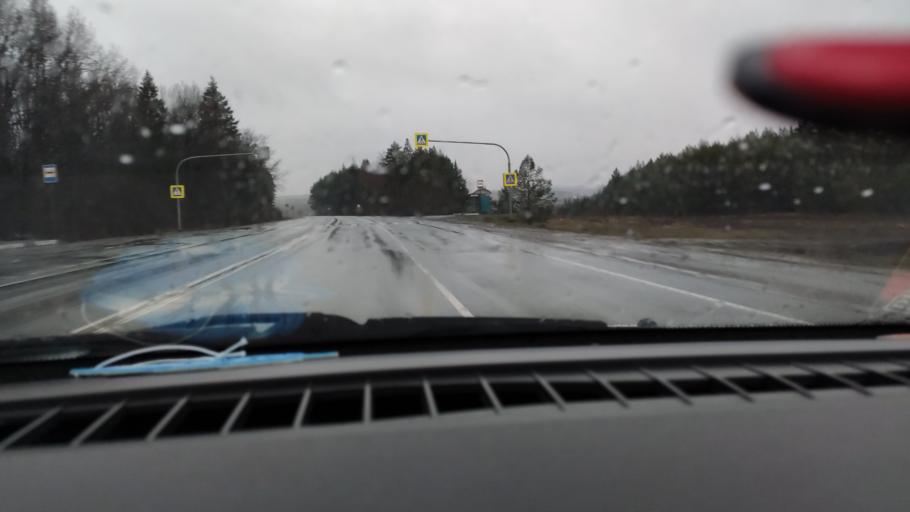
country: RU
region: Tatarstan
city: Mendeleyevsk
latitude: 55.9428
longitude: 52.2928
